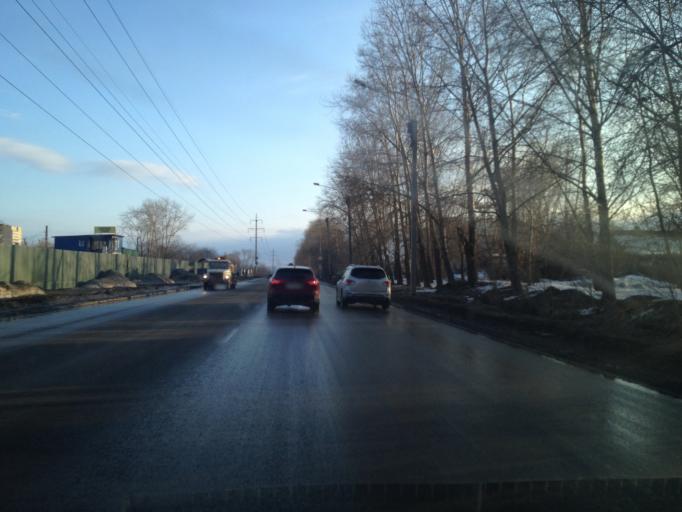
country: RU
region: Sverdlovsk
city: Sovkhoznyy
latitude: 56.7707
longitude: 60.5963
